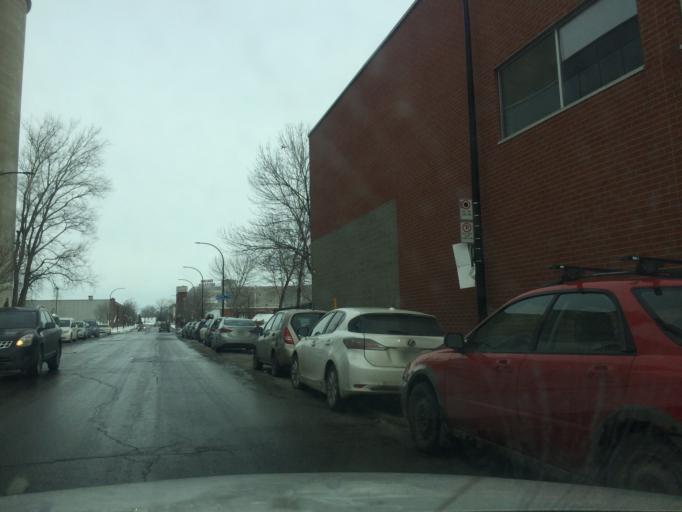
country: CA
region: Quebec
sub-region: Montreal
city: Montreal
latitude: 45.4864
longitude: -73.5614
